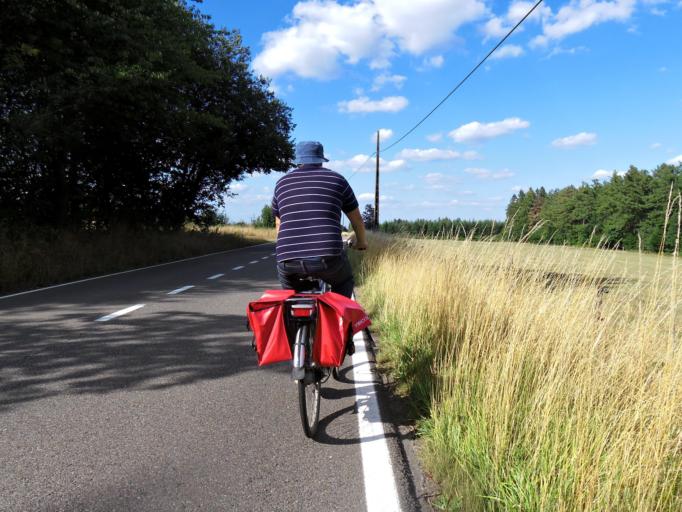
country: BE
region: Wallonia
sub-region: Province de Namur
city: Bievre
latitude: 49.9252
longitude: 5.0411
